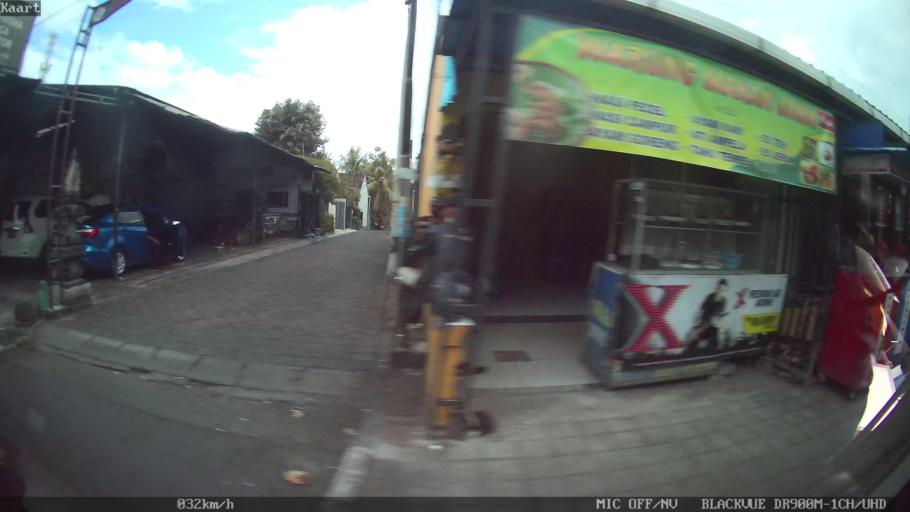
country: ID
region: Bali
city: Banjar Pekenjelodan
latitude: -8.5832
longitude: 115.1804
